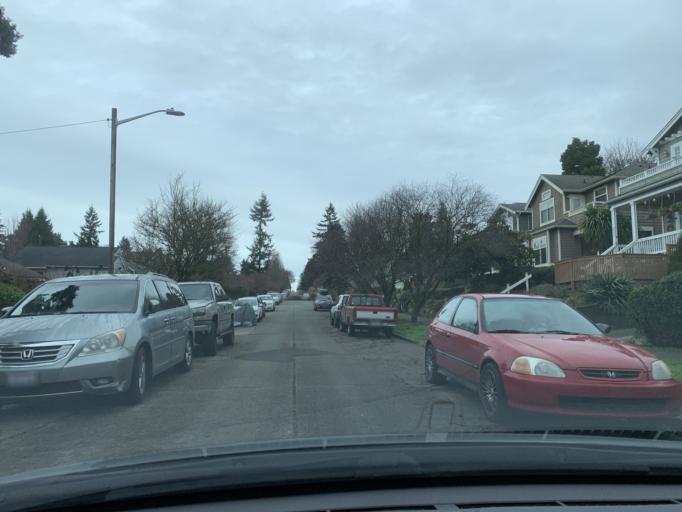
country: US
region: Washington
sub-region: King County
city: White Center
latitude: 47.5621
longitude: -122.3921
